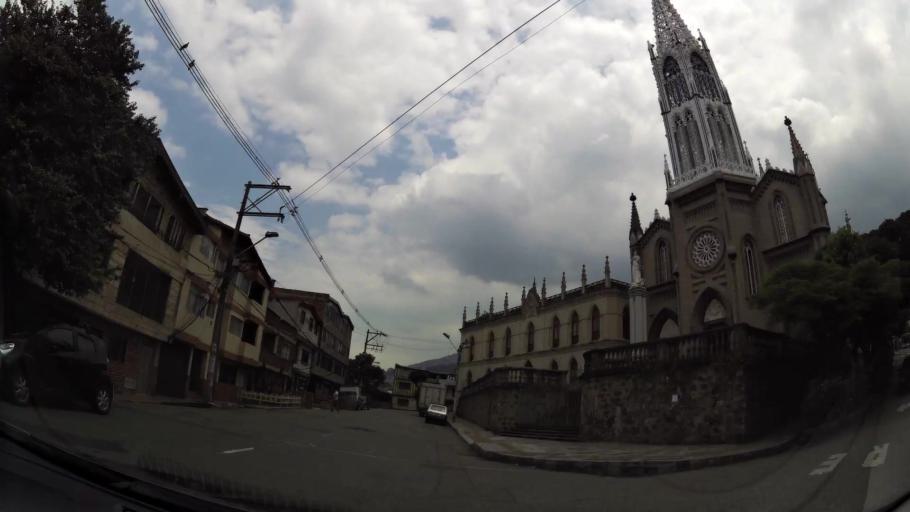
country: CO
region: Antioquia
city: Medellin
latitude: 6.2633
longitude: -75.5575
